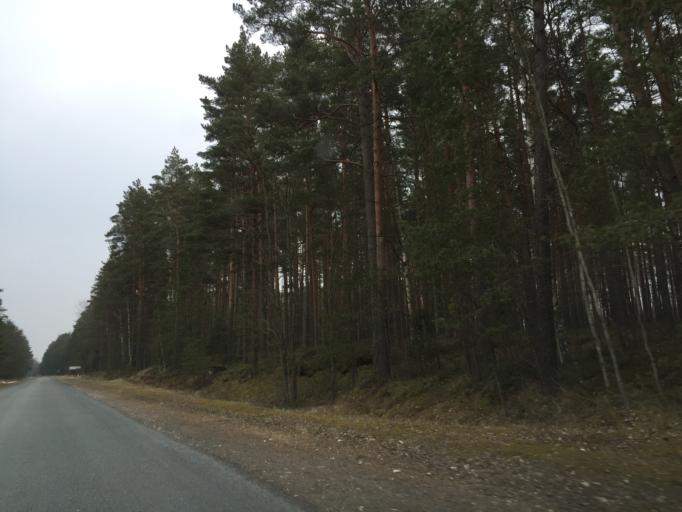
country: LV
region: Salacgrivas
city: Ainazi
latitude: 57.9899
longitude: 24.4252
